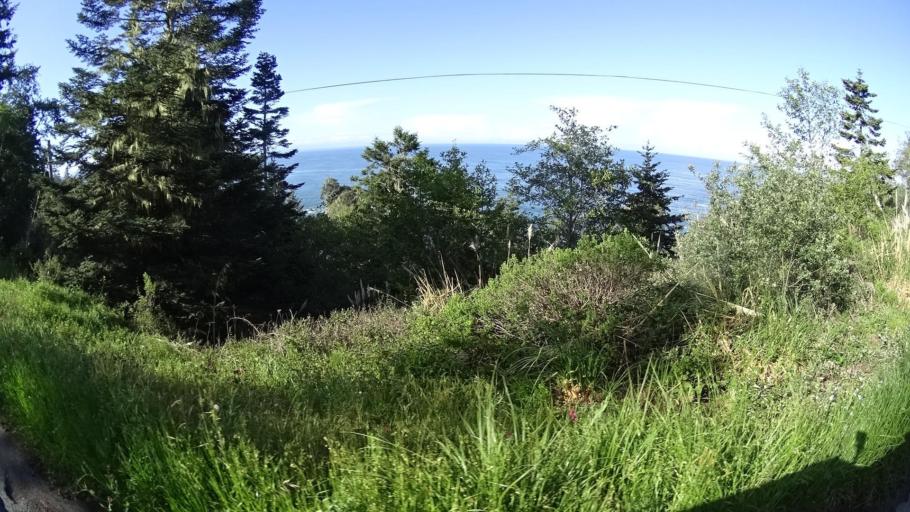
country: US
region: California
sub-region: Humboldt County
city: Westhaven-Moonstone
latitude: 41.0521
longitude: -124.1285
